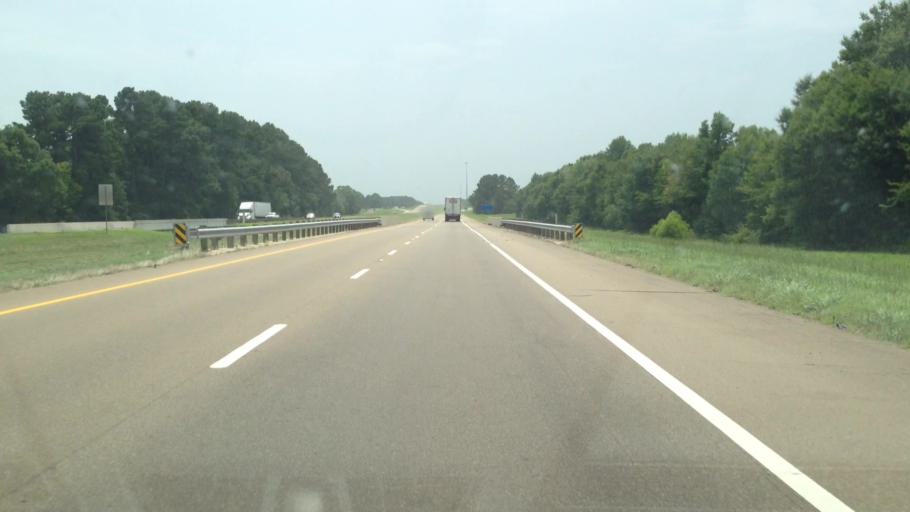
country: US
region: Texas
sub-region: Bowie County
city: De Kalb
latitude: 33.4244
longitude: -94.5464
